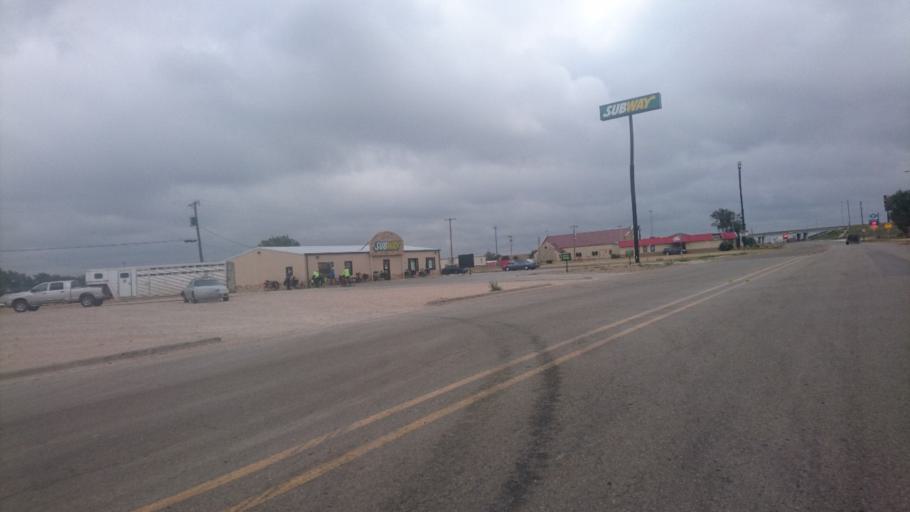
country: US
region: Texas
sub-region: Oldham County
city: Vega
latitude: 35.2406
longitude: -102.4285
